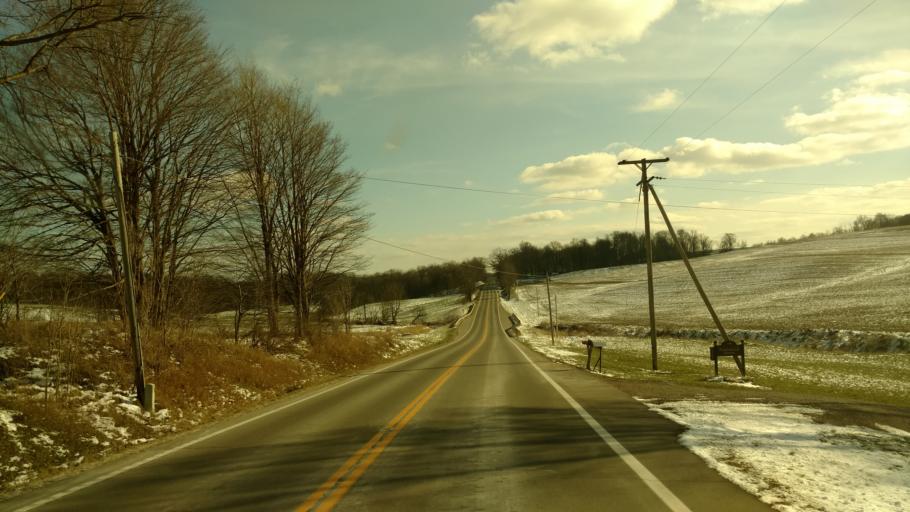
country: US
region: Ohio
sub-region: Ashland County
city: Loudonville
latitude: 40.7247
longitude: -82.2408
